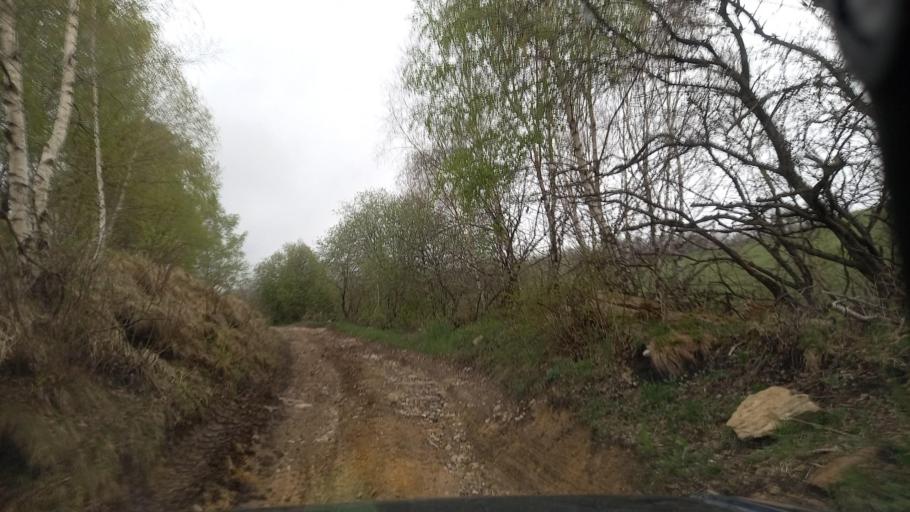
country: RU
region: Stavropol'skiy
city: Nezhinskiy
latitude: 43.8543
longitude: 42.6363
